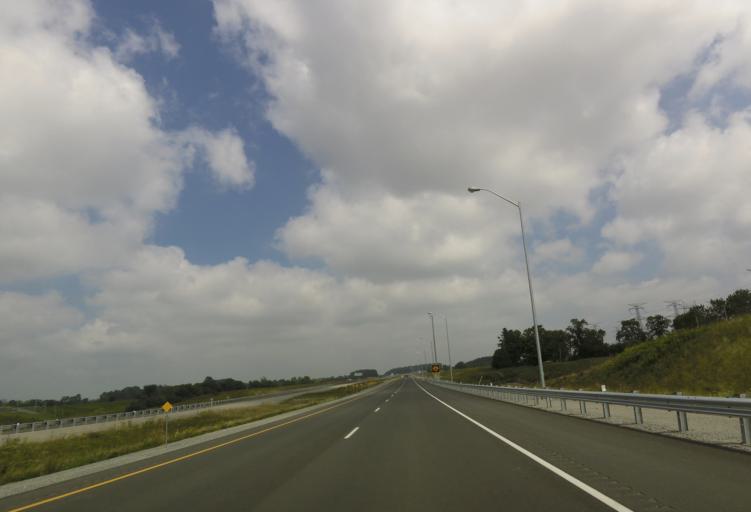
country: CA
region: Ontario
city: Oshawa
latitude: 43.9768
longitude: -78.8881
